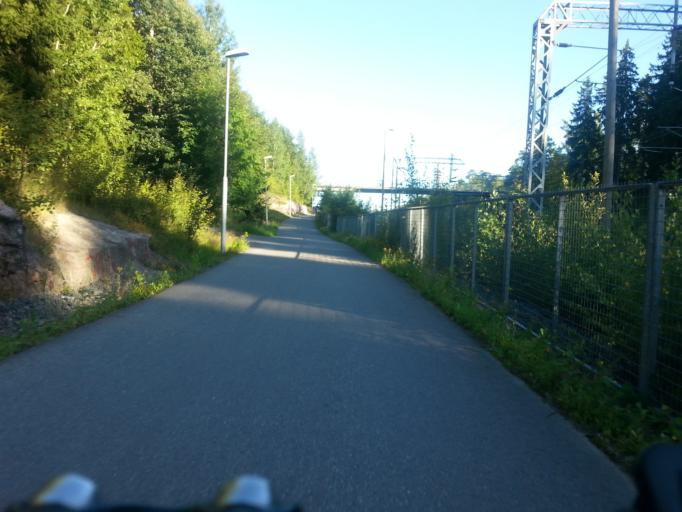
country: FI
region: Uusimaa
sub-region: Helsinki
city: Helsinki
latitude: 60.2123
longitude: 24.9125
